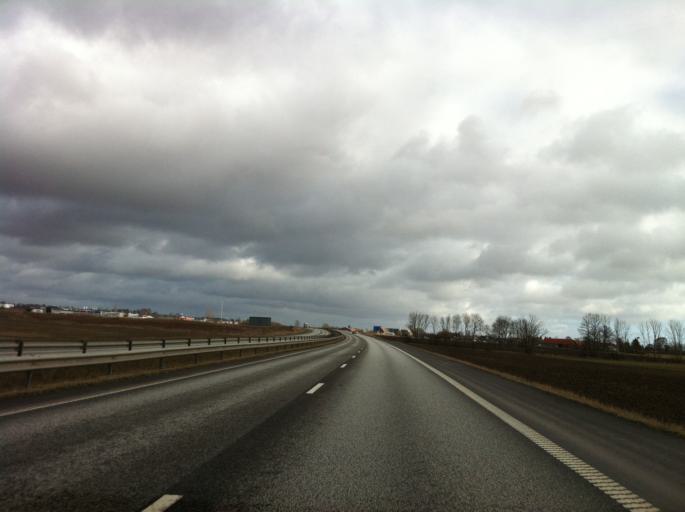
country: SE
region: Skane
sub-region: Kristianstads Kommun
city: Onnestad
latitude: 56.0296
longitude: 14.0796
